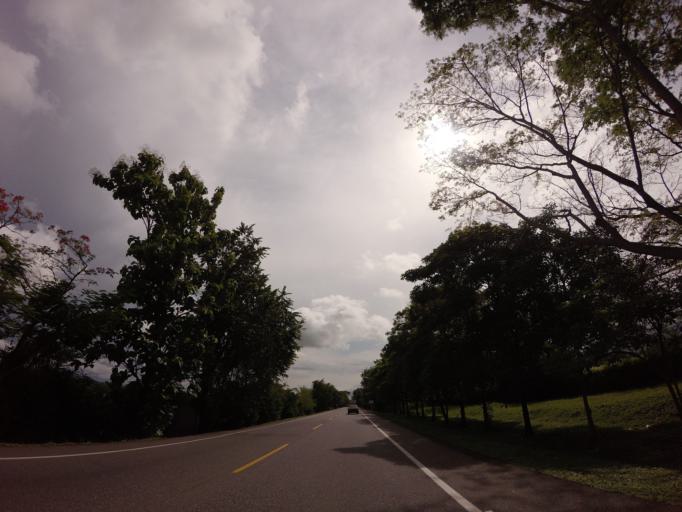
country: CO
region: Caldas
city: La Dorada
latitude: 5.3574
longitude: -74.7261
